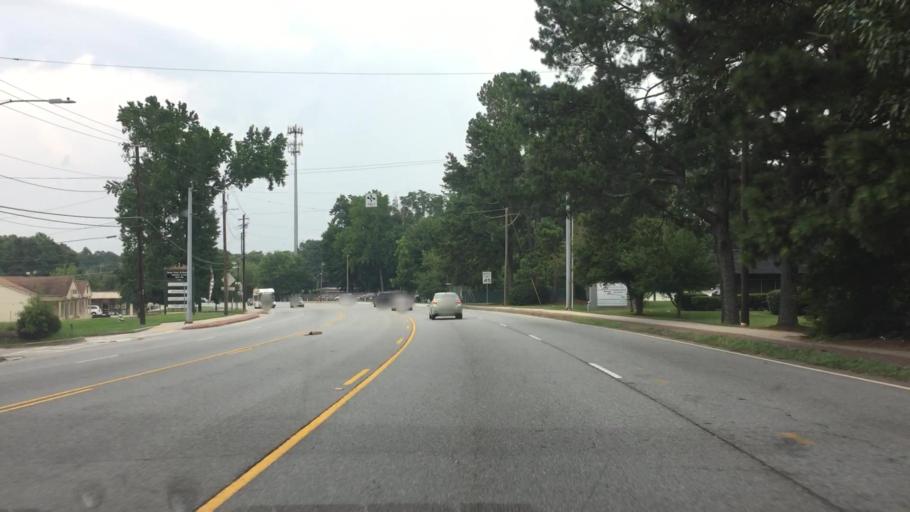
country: US
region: Georgia
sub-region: DeKalb County
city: Avondale Estates
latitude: 33.7641
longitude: -84.2511
